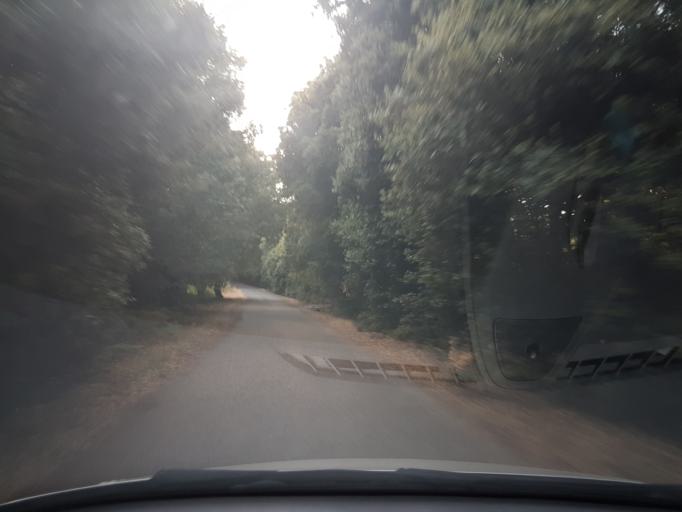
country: IT
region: Sardinia
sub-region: Provincia di Oristano
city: Seneghe
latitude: 40.1139
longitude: 8.5807
